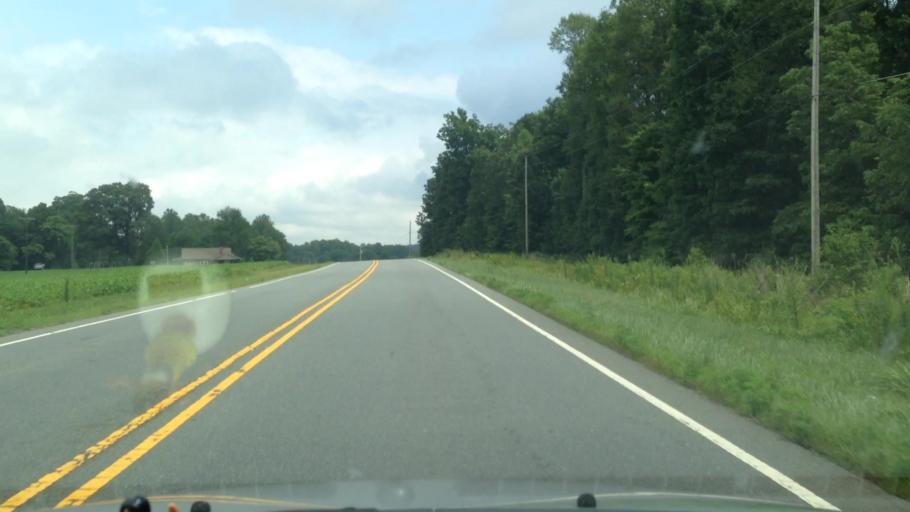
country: US
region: North Carolina
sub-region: Forsyth County
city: Walkertown
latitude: 36.1944
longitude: -80.0932
